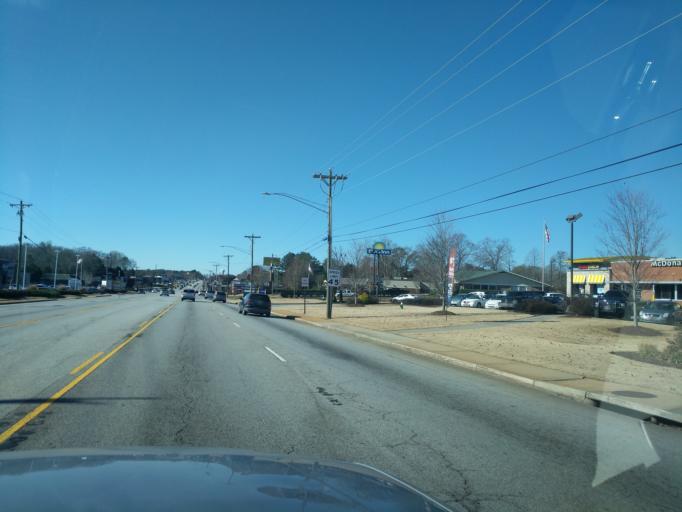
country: US
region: South Carolina
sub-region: Pickens County
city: Easley
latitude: 34.8264
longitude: -82.5663
